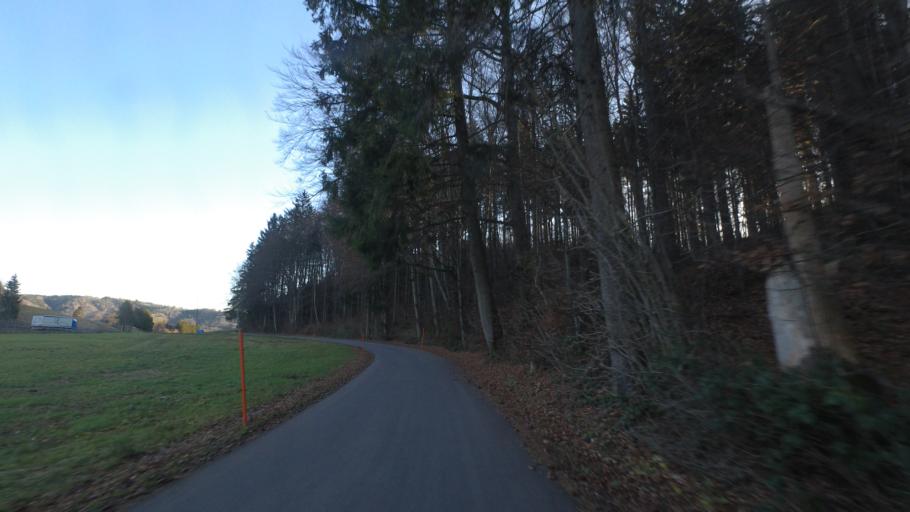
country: DE
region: Bavaria
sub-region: Upper Bavaria
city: Vachendorf
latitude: 47.8266
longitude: 12.6193
